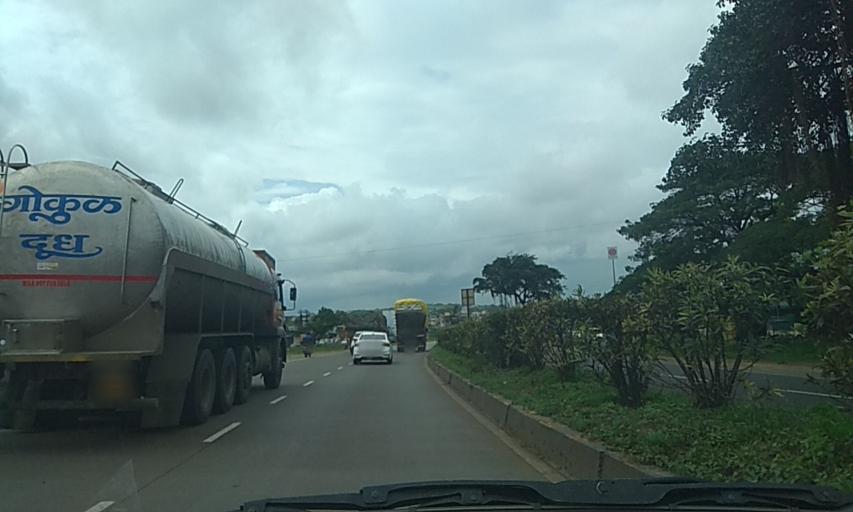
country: IN
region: Maharashtra
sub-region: Kolhapur
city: Kagal
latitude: 16.6393
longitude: 74.2779
